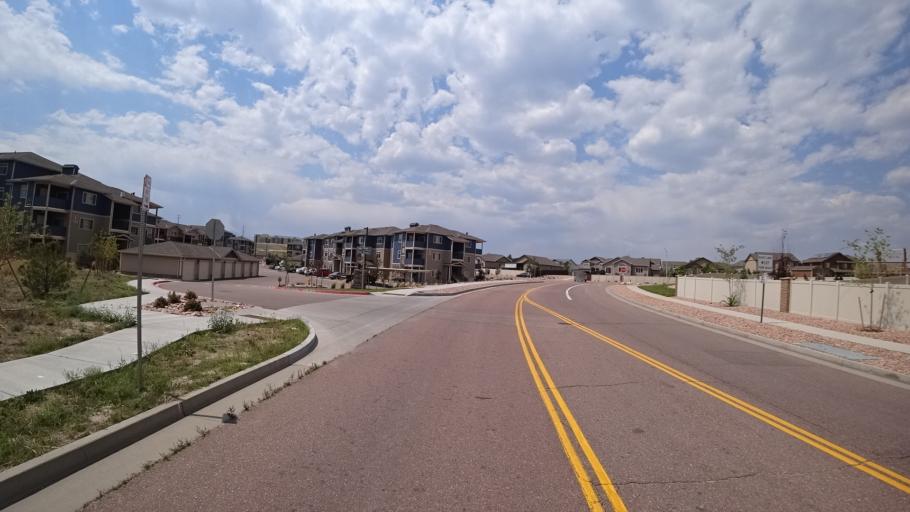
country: US
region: Colorado
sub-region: El Paso County
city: Black Forest
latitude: 38.9438
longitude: -104.6975
